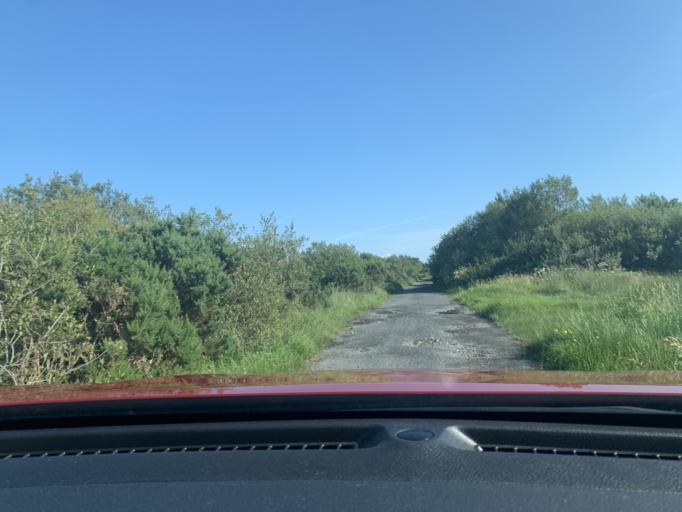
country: IE
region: Connaught
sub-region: Sligo
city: Tobercurry
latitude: 54.0654
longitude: -8.7924
